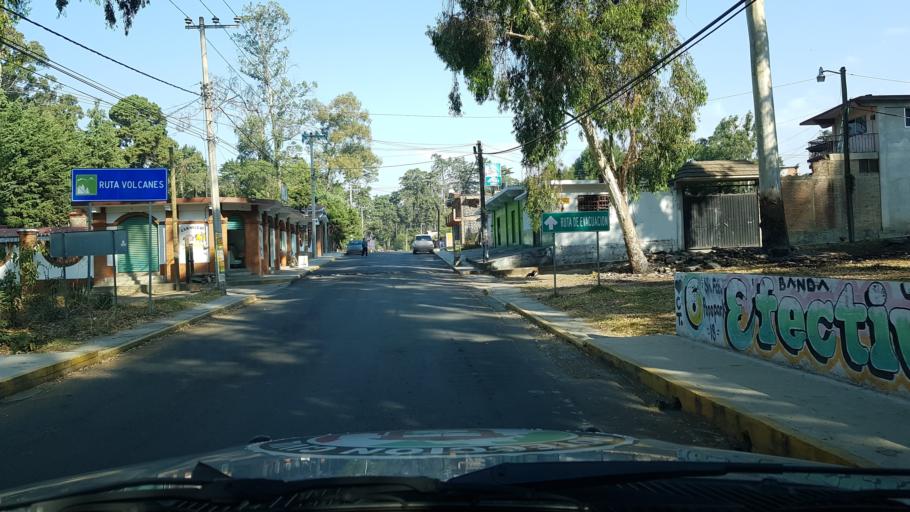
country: MX
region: Mexico
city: Ozumba de Alzate
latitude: 19.0590
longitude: -98.7779
